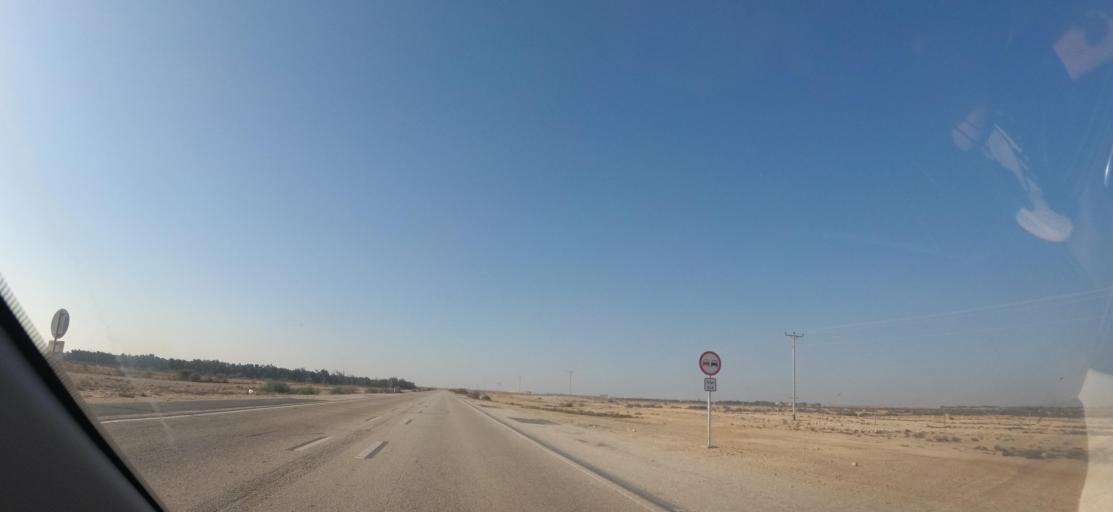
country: QA
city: Al Ghuwayriyah
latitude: 25.8500
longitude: 51.2634
